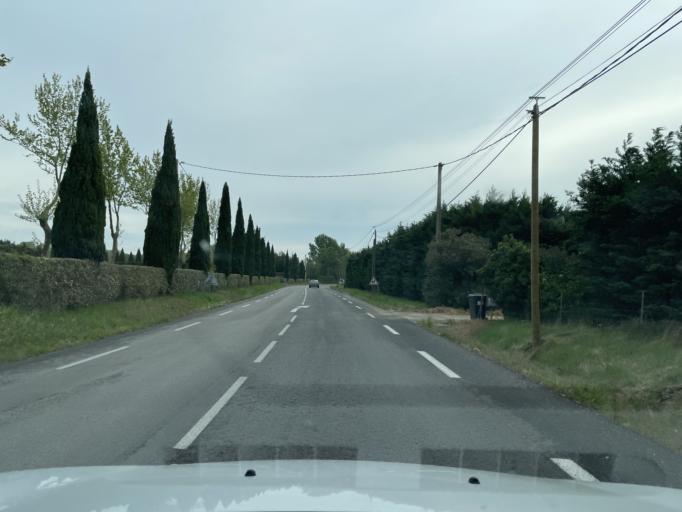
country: FR
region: Provence-Alpes-Cote d'Azur
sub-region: Departement des Bouches-du-Rhone
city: Tarascon
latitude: 43.8169
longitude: 4.6791
